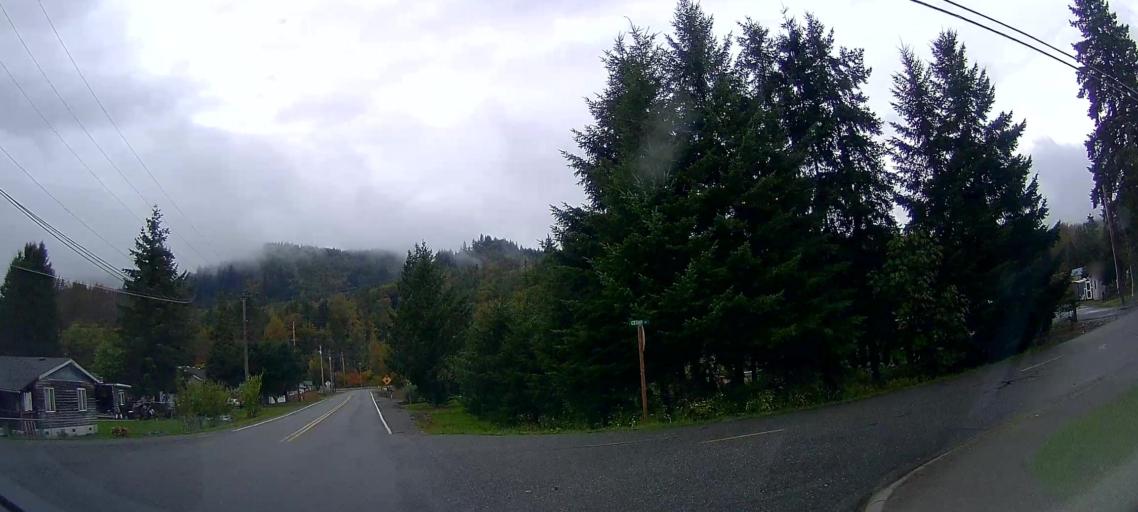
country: US
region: Washington
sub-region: Snohomish County
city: Darrington
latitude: 48.5345
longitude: -121.7660
